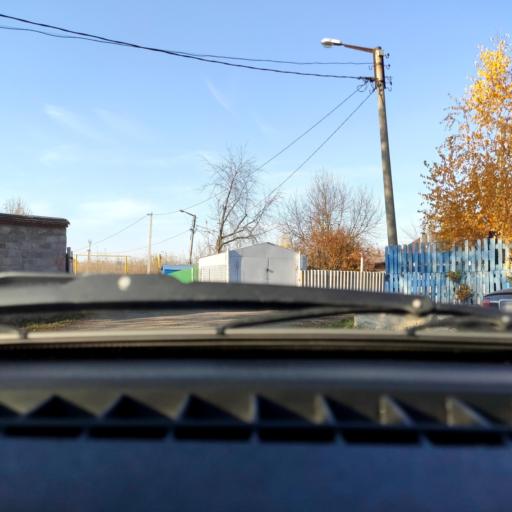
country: RU
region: Bashkortostan
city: Ufa
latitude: 54.8227
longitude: 56.1256
